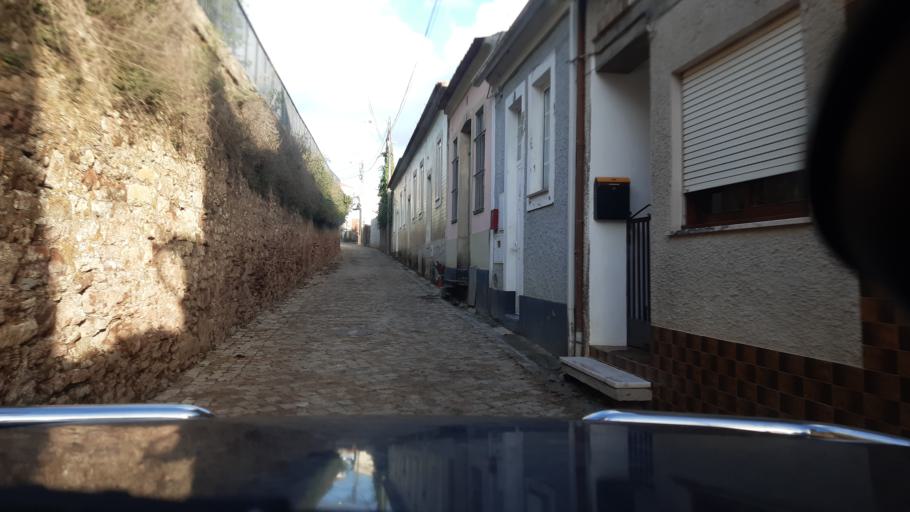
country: PT
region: Aveiro
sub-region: Agueda
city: Agueda
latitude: 40.5728
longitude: -8.4497
